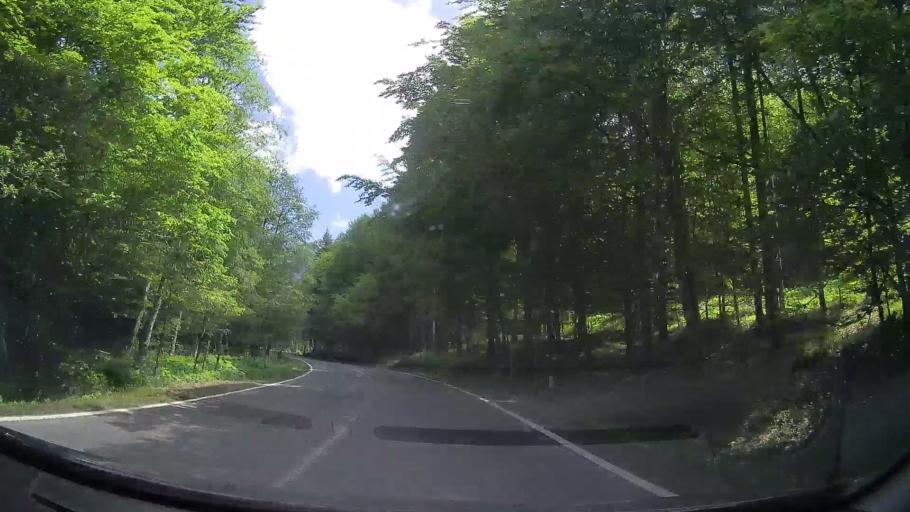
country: RO
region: Brasov
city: Crivina
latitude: 45.4580
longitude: 25.9523
